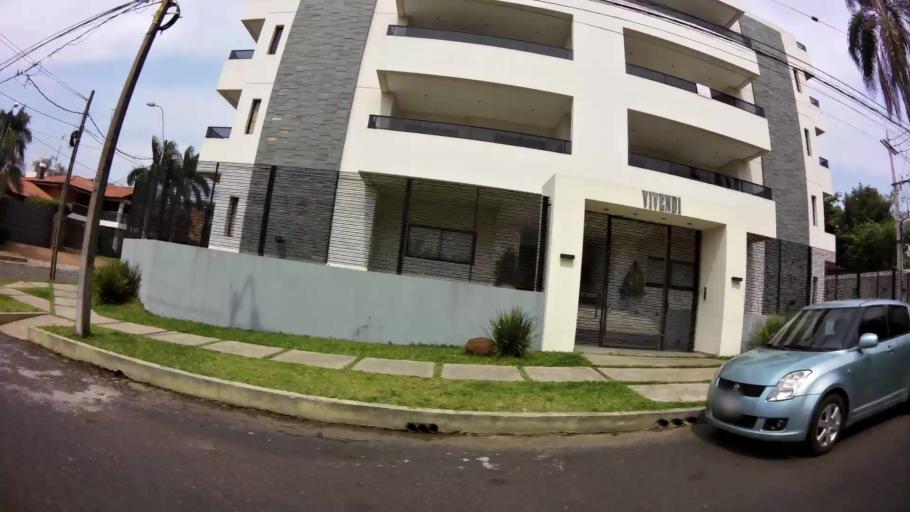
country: PY
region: Asuncion
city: Asuncion
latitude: -25.2811
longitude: -57.5796
